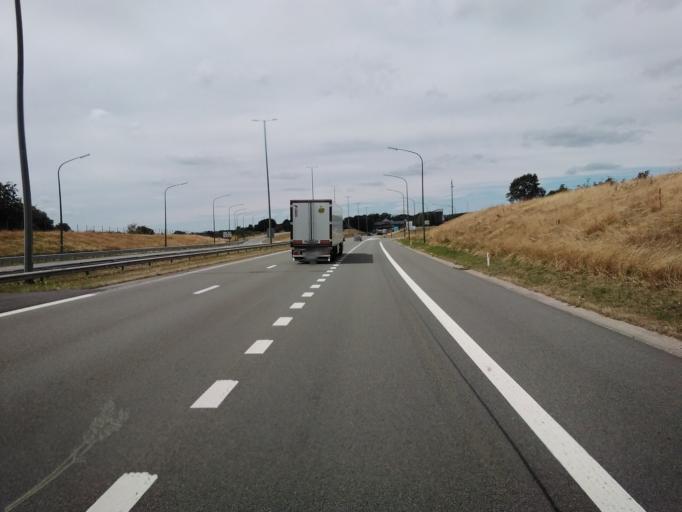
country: BE
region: Wallonia
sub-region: Province du Luxembourg
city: Arlon
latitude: 49.6405
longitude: 5.8385
